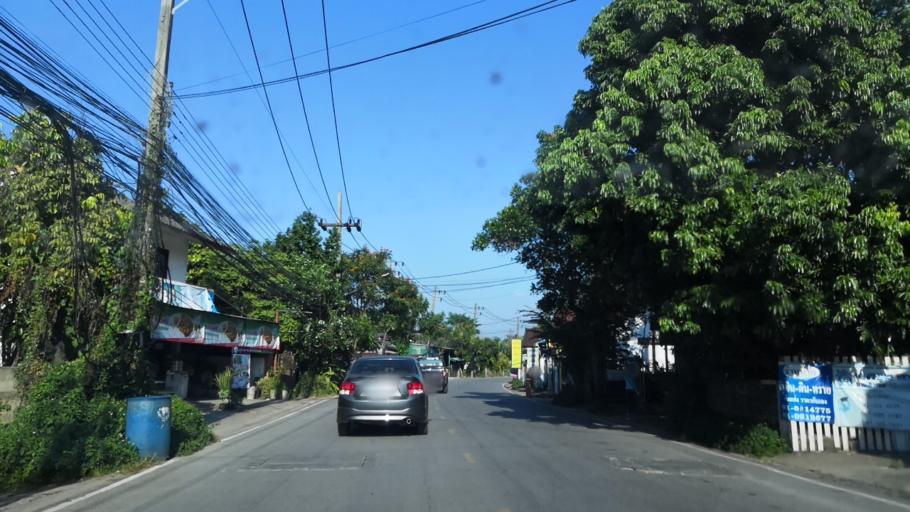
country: TH
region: Chiang Rai
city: Chiang Rai
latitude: 19.9288
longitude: 99.8488
